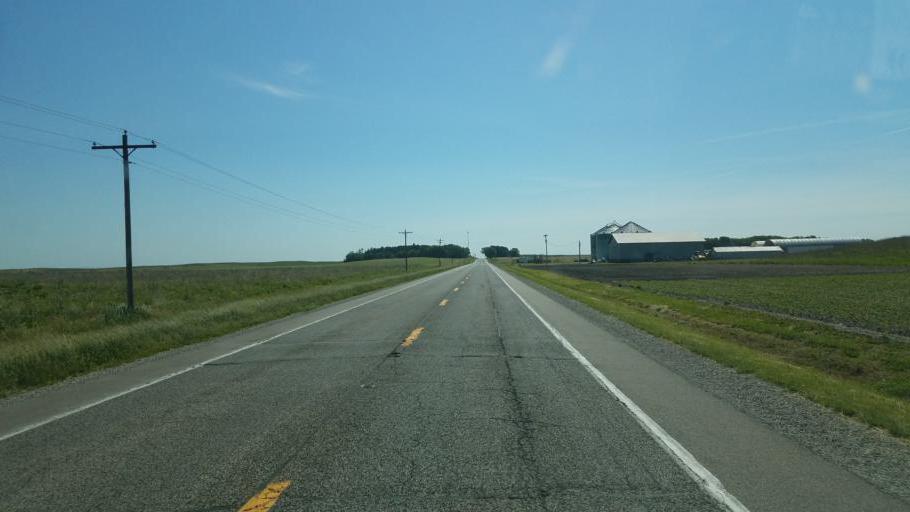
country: US
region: Illinois
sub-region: Mason County
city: Manito
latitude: 40.3033
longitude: -89.7935
